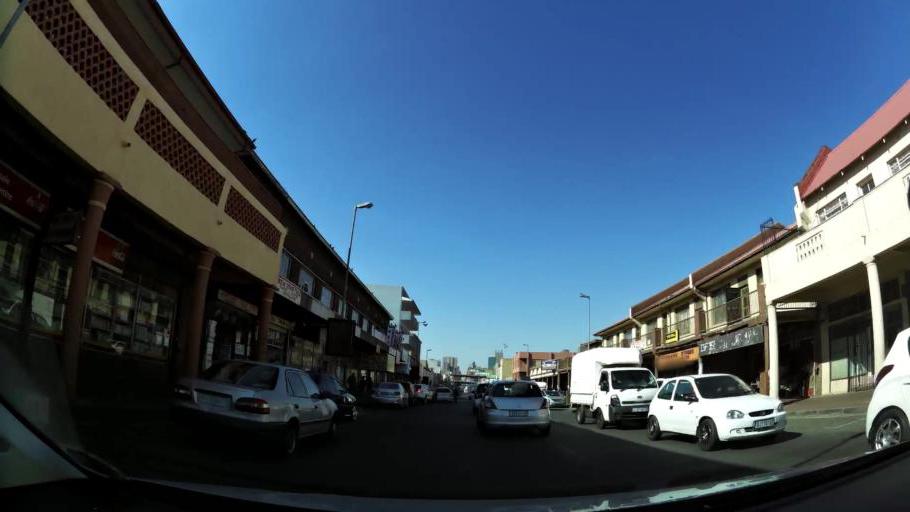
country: ZA
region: Gauteng
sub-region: City of Johannesburg Metropolitan Municipality
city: Johannesburg
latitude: -26.2027
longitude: 28.0257
